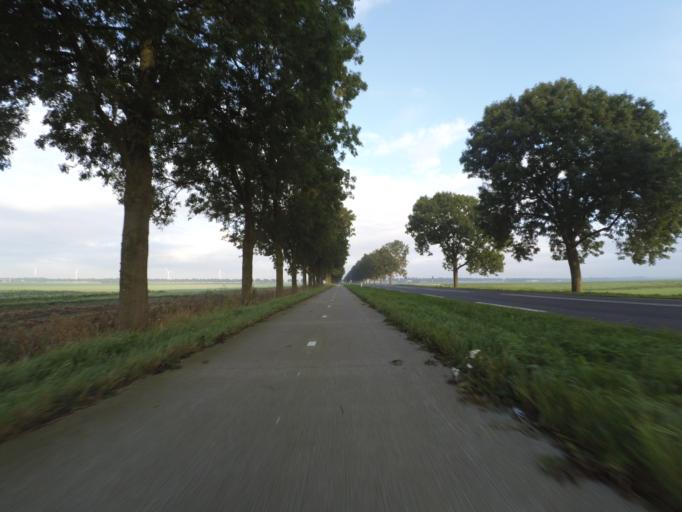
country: NL
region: Flevoland
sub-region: Gemeente Dronten
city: Biddinghuizen
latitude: 52.4757
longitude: 5.6732
